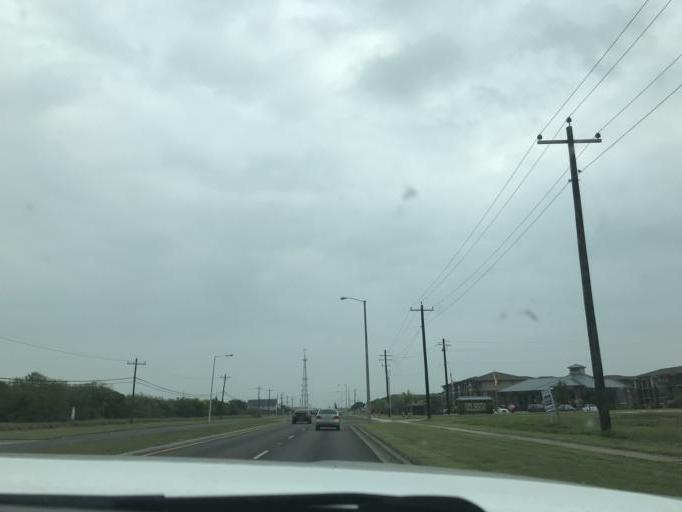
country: US
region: Texas
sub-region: Nueces County
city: Corpus Christi
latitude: 27.6742
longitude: -97.3612
